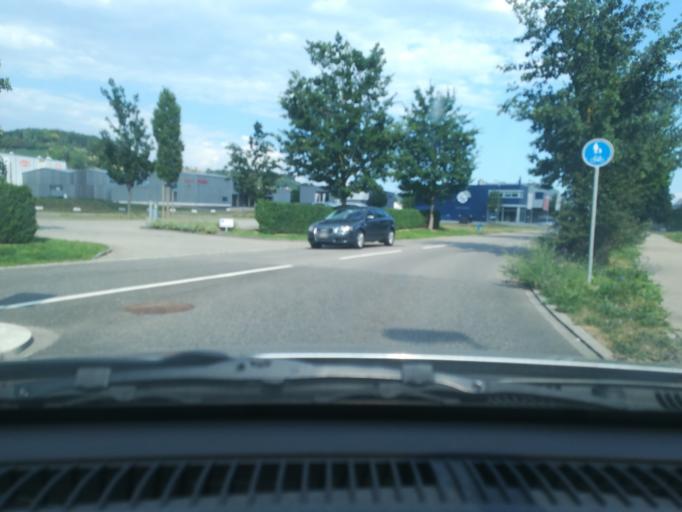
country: CH
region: Schaffhausen
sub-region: Bezirk Reiat
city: Thayngen
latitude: 47.7439
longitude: 8.7059
